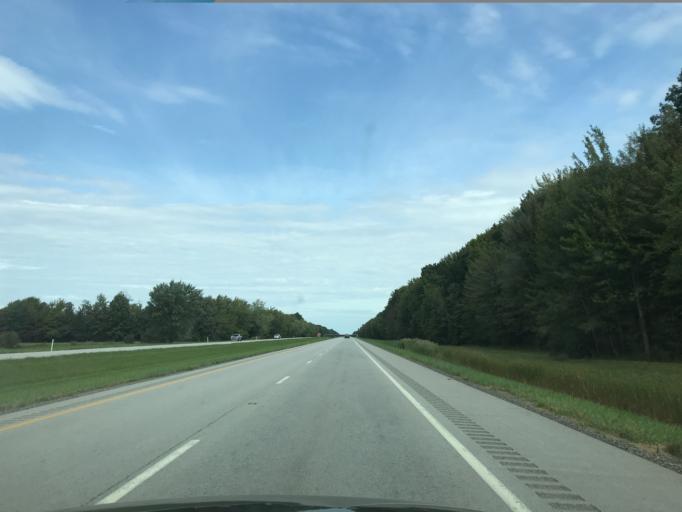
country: US
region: Ohio
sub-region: Ashtabula County
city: Roaming Shores
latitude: 41.6413
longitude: -80.7133
